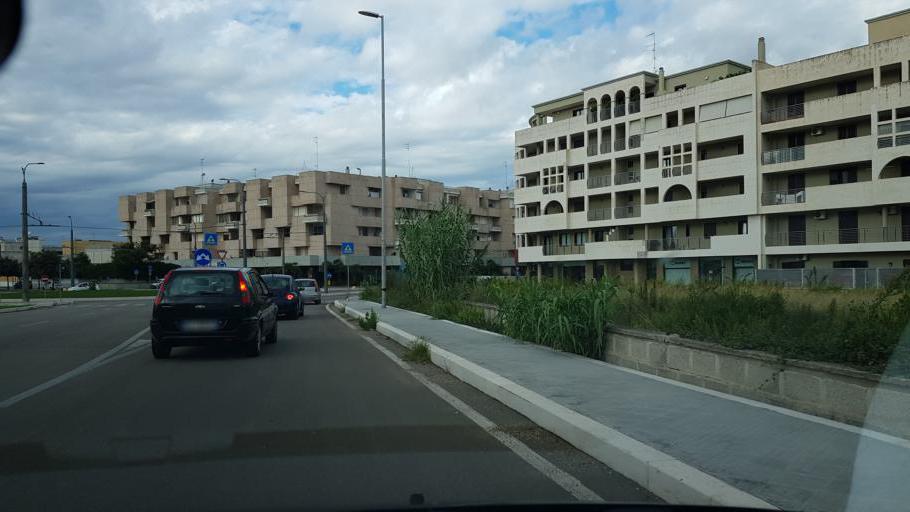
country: IT
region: Apulia
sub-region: Provincia di Lecce
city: Lecce
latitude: 40.3454
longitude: 18.1838
